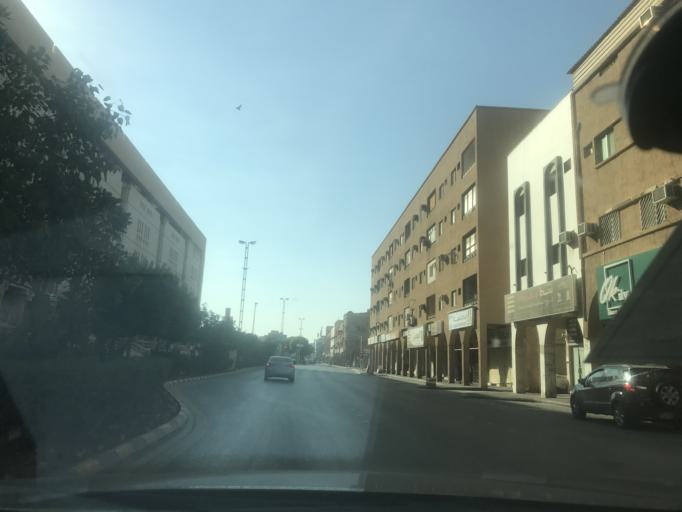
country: SA
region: Ar Riyad
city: Riyadh
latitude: 24.6313
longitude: 46.7086
